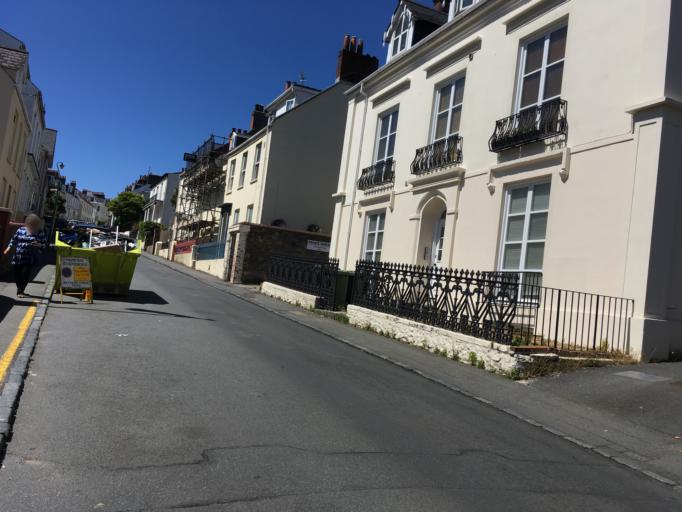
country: GG
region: St Peter Port
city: Saint Peter Port
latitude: 49.4538
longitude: -2.5442
